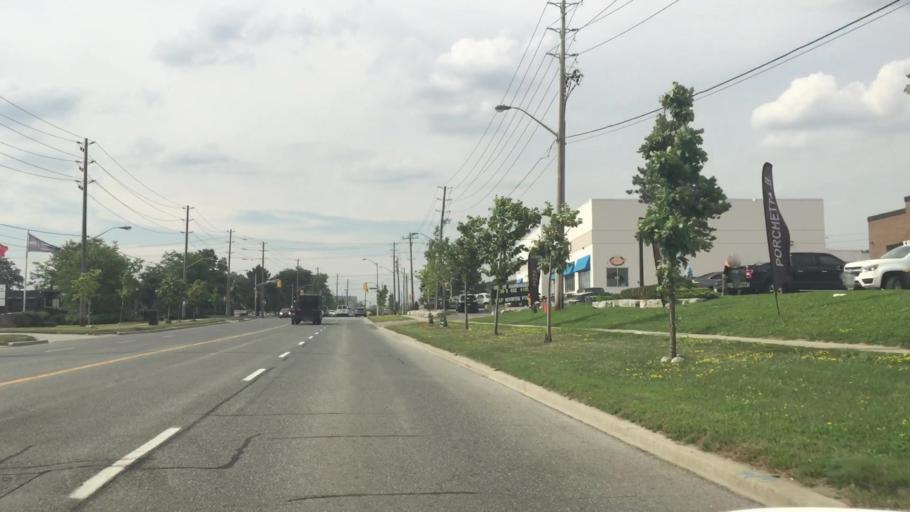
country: CA
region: Ontario
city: Concord
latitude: 43.7571
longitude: -79.5382
